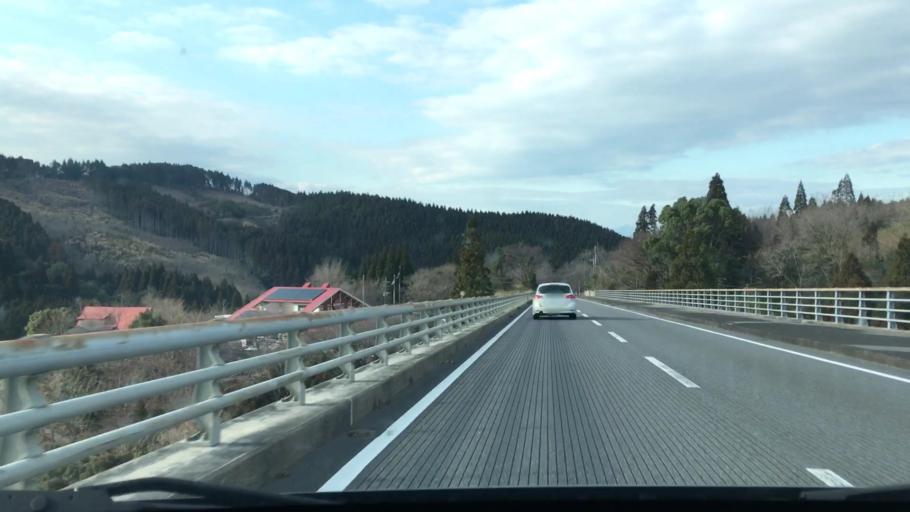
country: JP
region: Miyazaki
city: Miyazaki-shi
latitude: 31.7996
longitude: 131.3035
